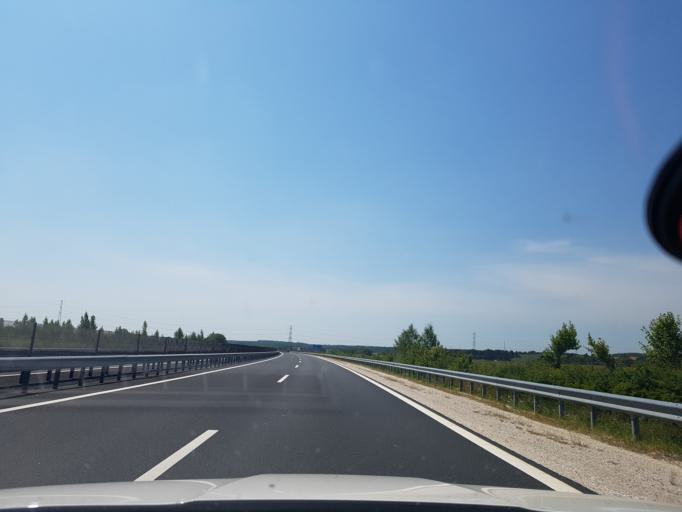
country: HU
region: Vas
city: Sarvar
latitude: 47.3101
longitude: 16.8390
